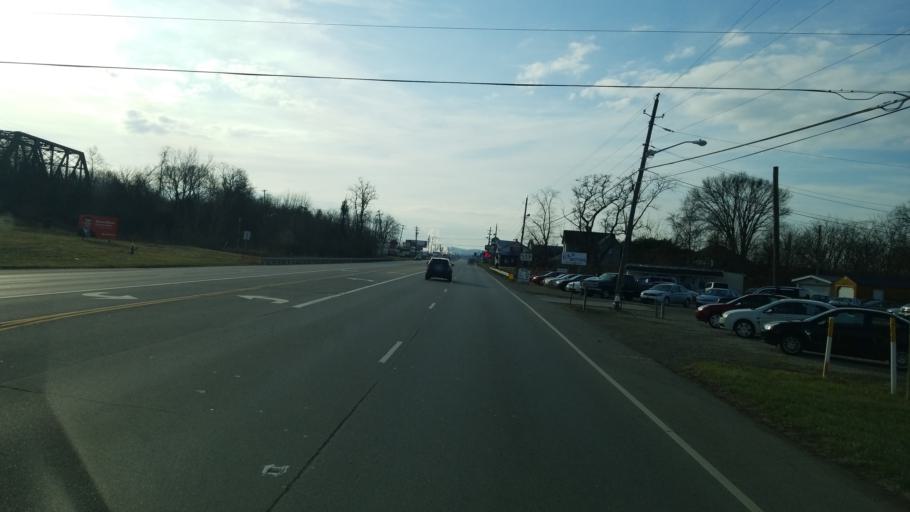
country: US
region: Ohio
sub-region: Ross County
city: Chillicothe
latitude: 39.3734
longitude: -82.9759
